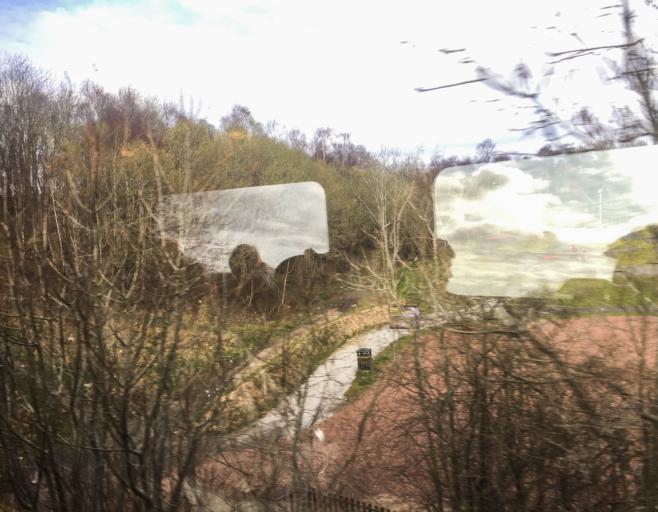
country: GB
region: Scotland
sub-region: North Lanarkshire
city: Wishaw
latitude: 55.7813
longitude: -3.9453
